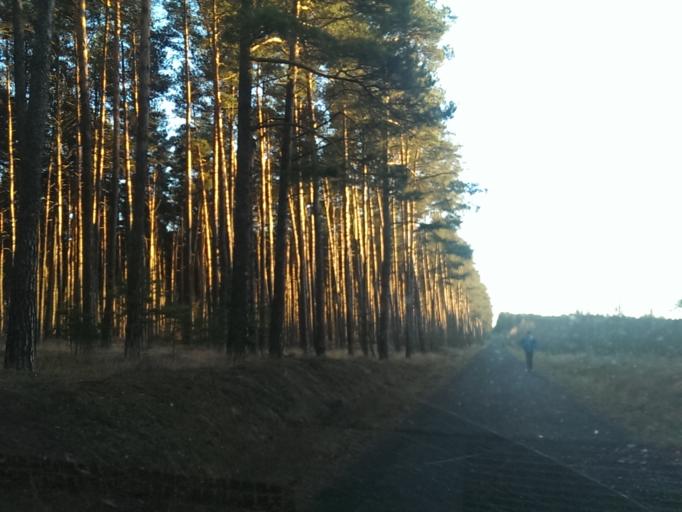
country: PL
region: Kujawsko-Pomorskie
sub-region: Powiat nakielski
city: Naklo nad Notecia
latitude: 53.0573
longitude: 17.5801
